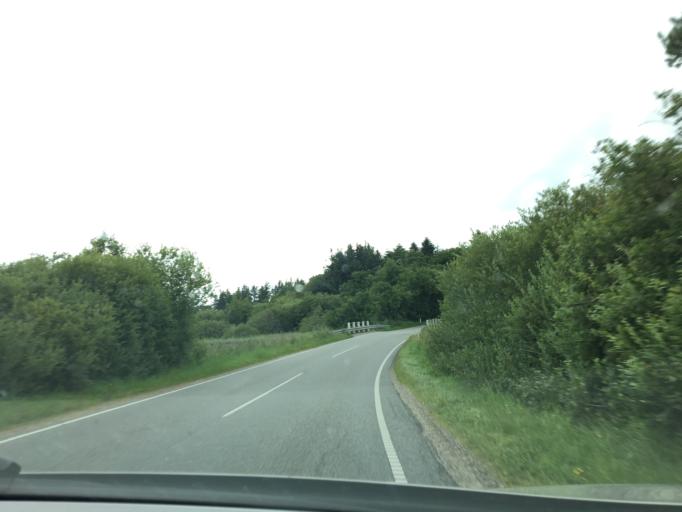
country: DK
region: South Denmark
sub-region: Varde Kommune
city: Oksbol
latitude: 55.6801
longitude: 8.3119
